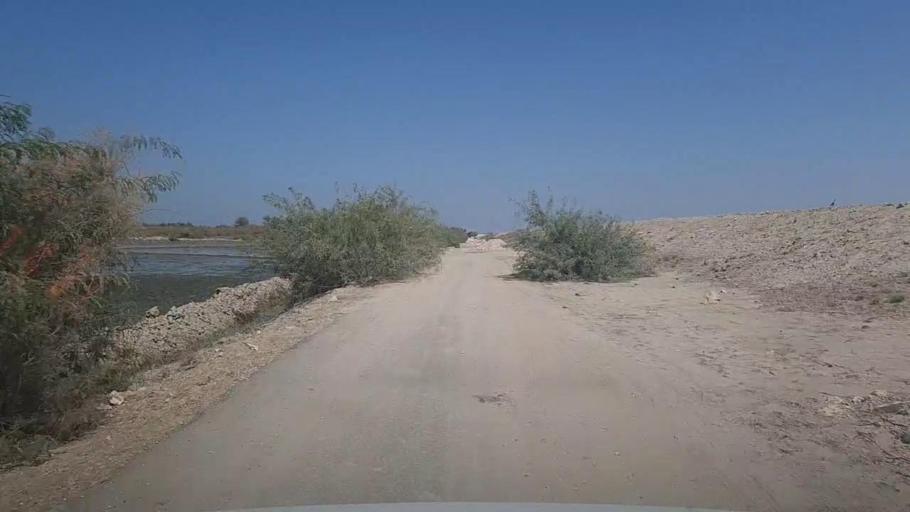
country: PK
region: Sindh
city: Kashmor
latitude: 28.2833
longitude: 69.4707
